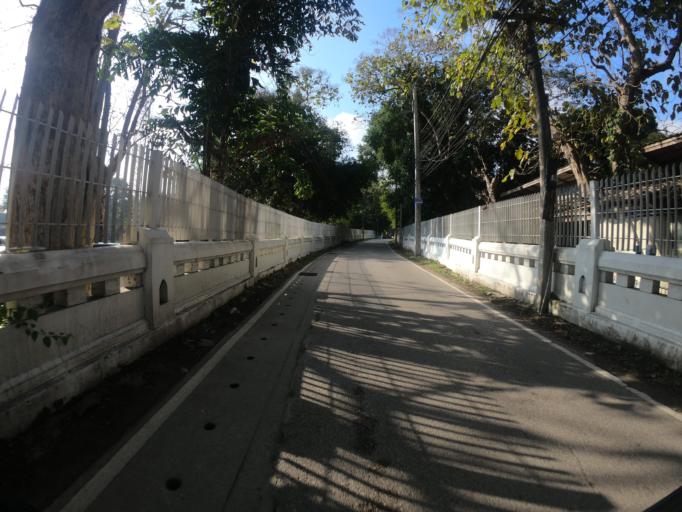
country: TH
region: Chiang Mai
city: Chiang Mai
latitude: 18.8120
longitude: 98.9550
